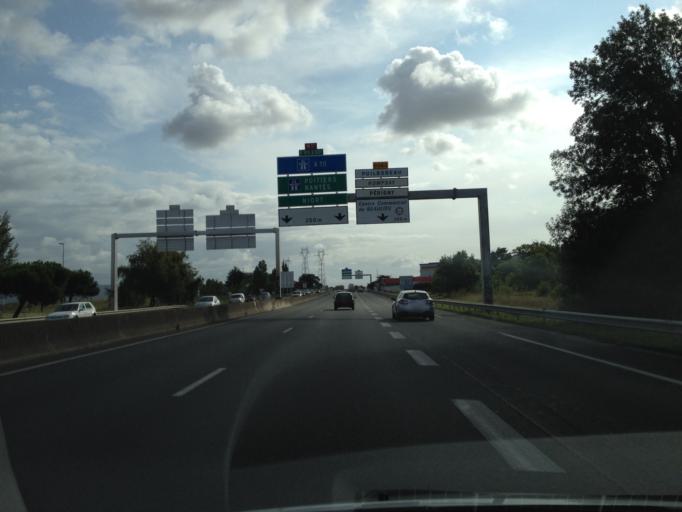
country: FR
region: Poitou-Charentes
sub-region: Departement de la Charente-Maritime
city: Puilboreau
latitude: 46.1733
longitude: -1.1160
